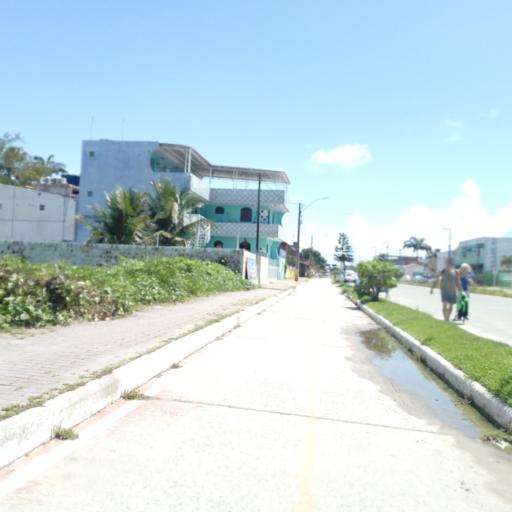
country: BR
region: Pernambuco
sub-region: Ipojuca
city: Ipojuca
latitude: -8.5087
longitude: -35.0087
